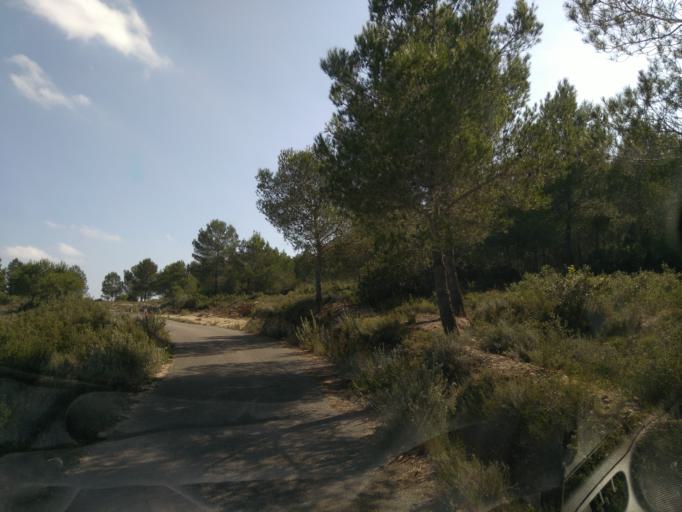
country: ES
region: Valencia
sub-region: Provincia de Valencia
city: Tous
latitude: 39.1814
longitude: -0.6331
